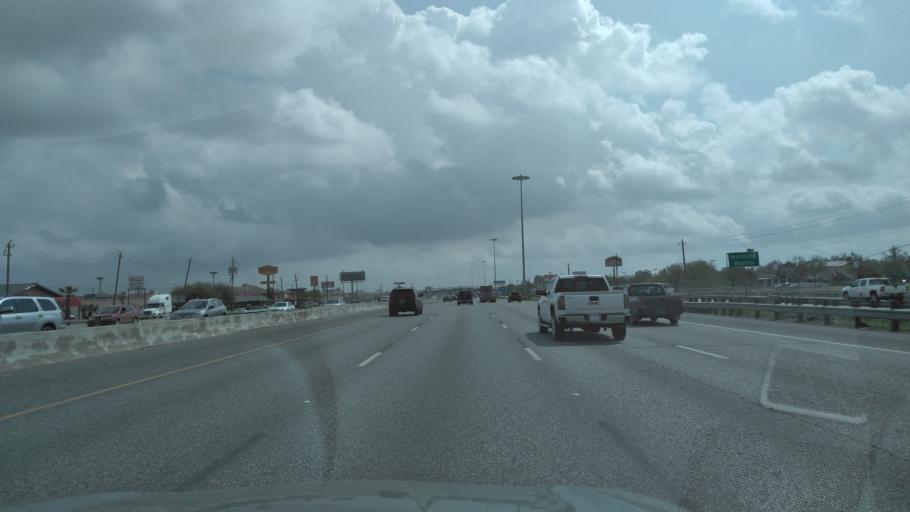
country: US
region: Texas
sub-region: Harris County
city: Jacinto City
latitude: 29.7721
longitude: -95.2285
